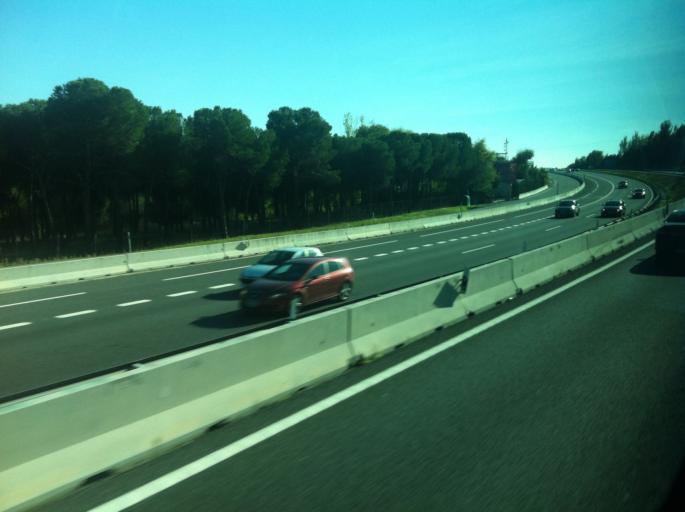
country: ES
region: Madrid
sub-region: Provincia de Madrid
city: San Agustin de Guadalix
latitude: 40.6847
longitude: -3.6097
